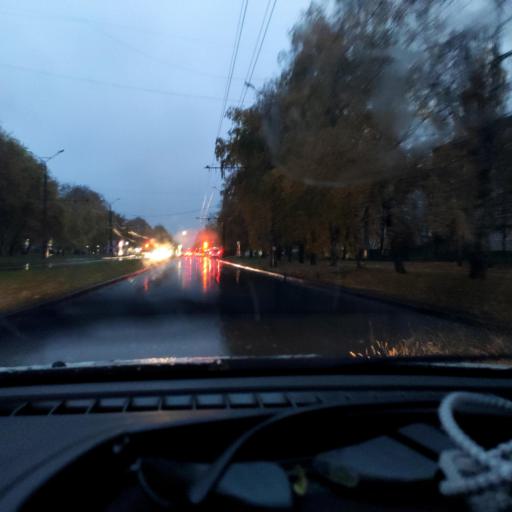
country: RU
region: Samara
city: Tol'yatti
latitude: 53.5325
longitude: 49.4289
